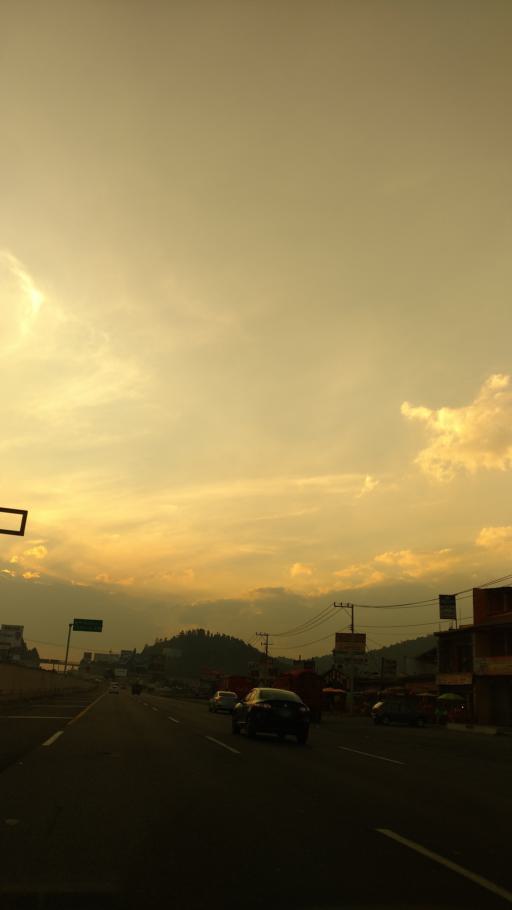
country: MX
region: Morelos
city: San Jeronimo Acazulco
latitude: 19.3005
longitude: -99.3823
